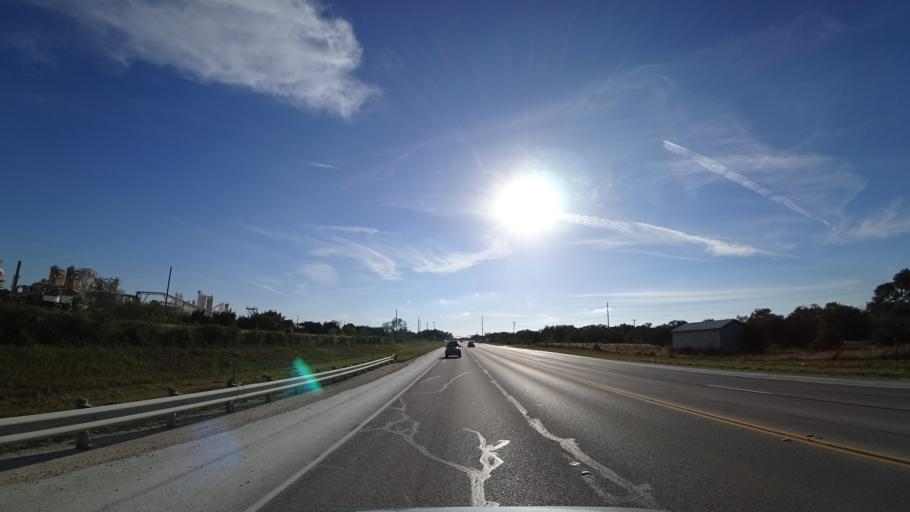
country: US
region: Texas
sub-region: Travis County
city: Wells Branch
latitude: 30.4589
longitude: -97.7187
